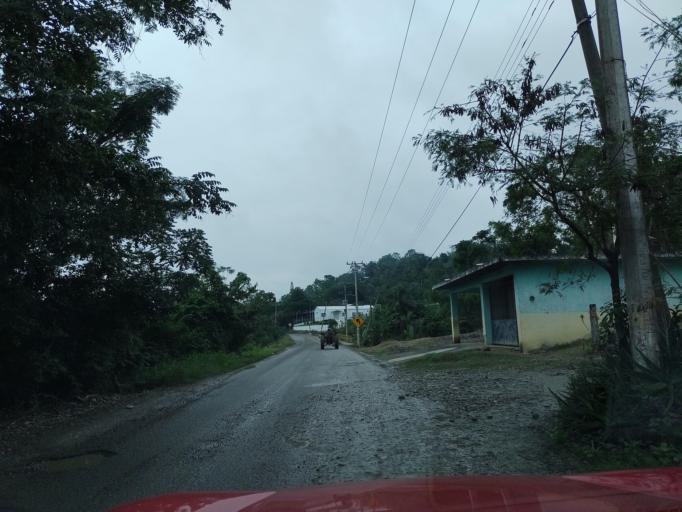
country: MX
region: Puebla
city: Espinal
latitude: 20.2622
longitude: -97.3696
